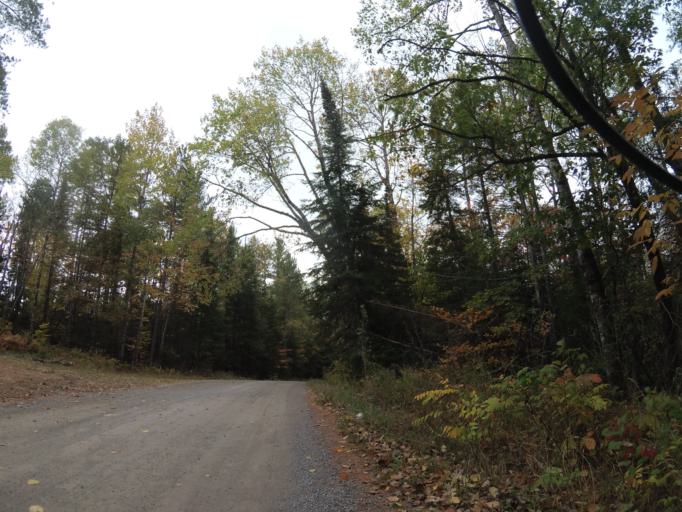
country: CA
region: Ontario
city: Renfrew
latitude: 45.2600
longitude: -77.2046
